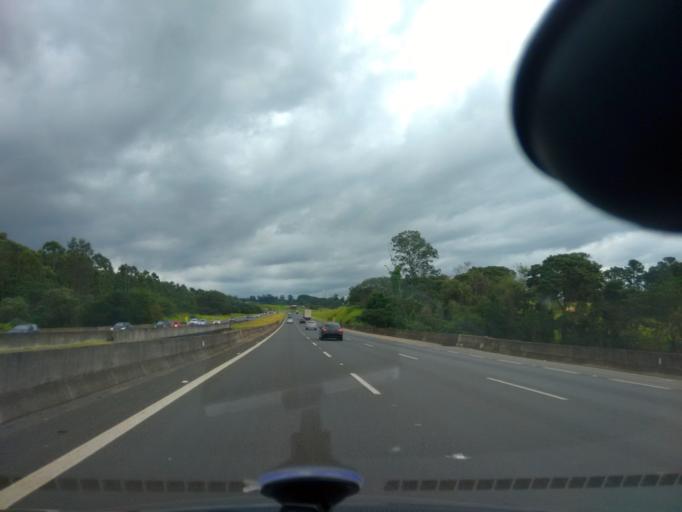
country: BR
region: Sao Paulo
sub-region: Hortolandia
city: Hortolandia
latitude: -22.9155
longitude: -47.1570
